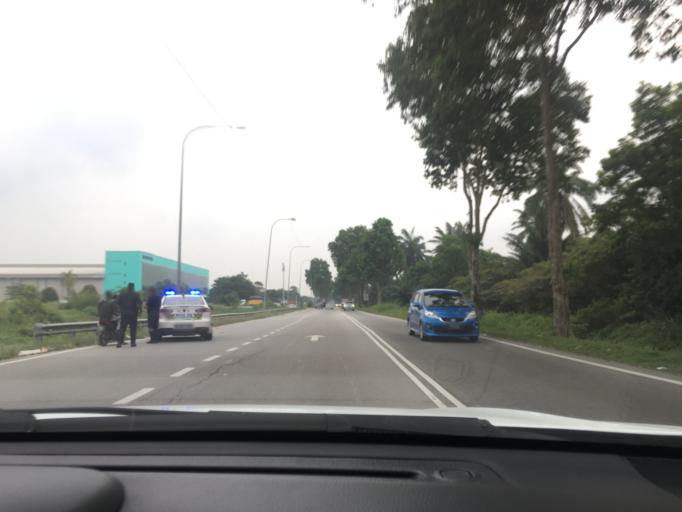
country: MY
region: Selangor
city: Klang
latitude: 3.1362
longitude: 101.4040
